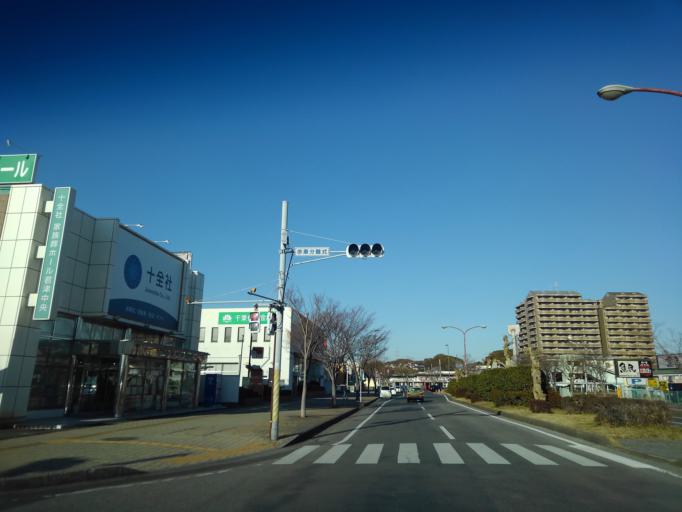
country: JP
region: Chiba
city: Kimitsu
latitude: 35.3323
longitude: 139.8937
